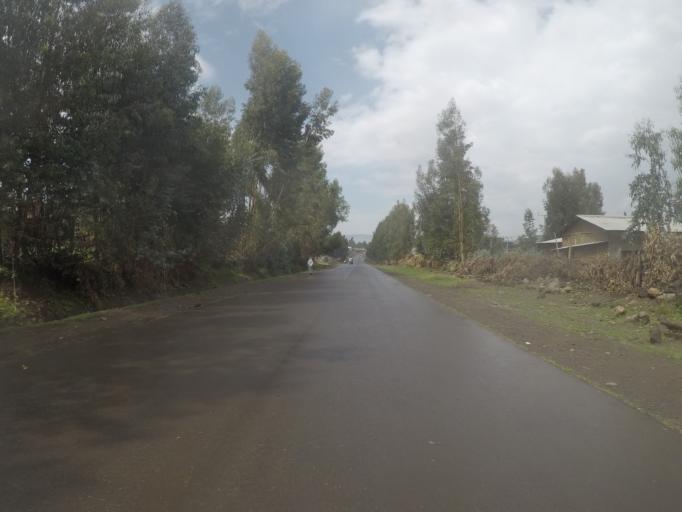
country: ET
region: Amhara
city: Debark'
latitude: 13.1209
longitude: 37.8825
